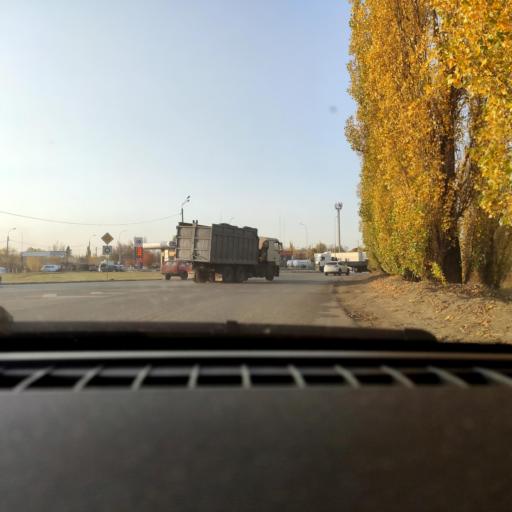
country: RU
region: Voronezj
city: Maslovka
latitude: 51.6230
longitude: 39.2609
